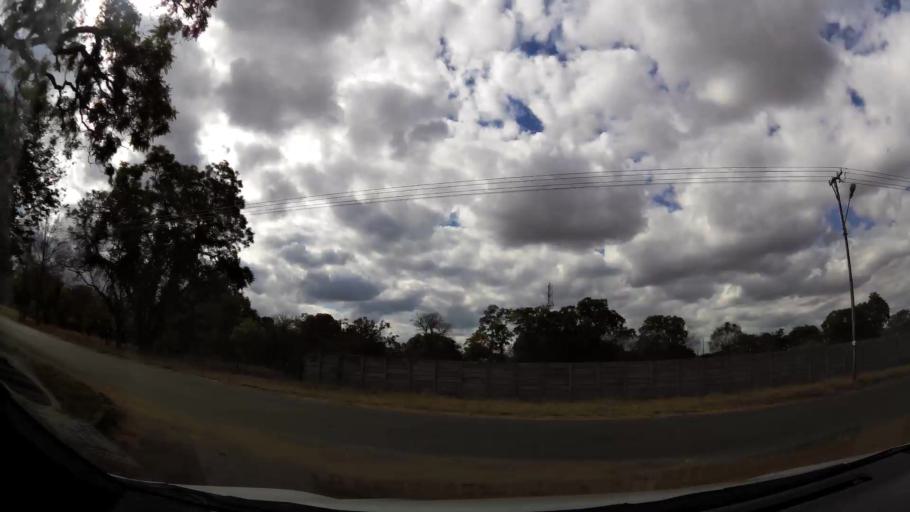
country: ZA
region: Limpopo
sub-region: Waterberg District Municipality
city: Modimolle
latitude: -24.7060
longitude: 28.4072
